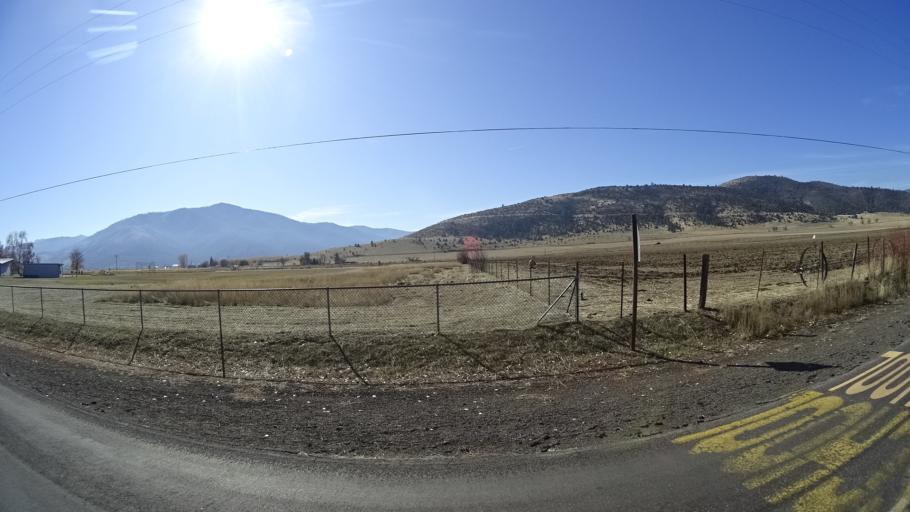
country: US
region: California
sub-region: Siskiyou County
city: Weed
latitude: 41.5215
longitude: -122.5245
